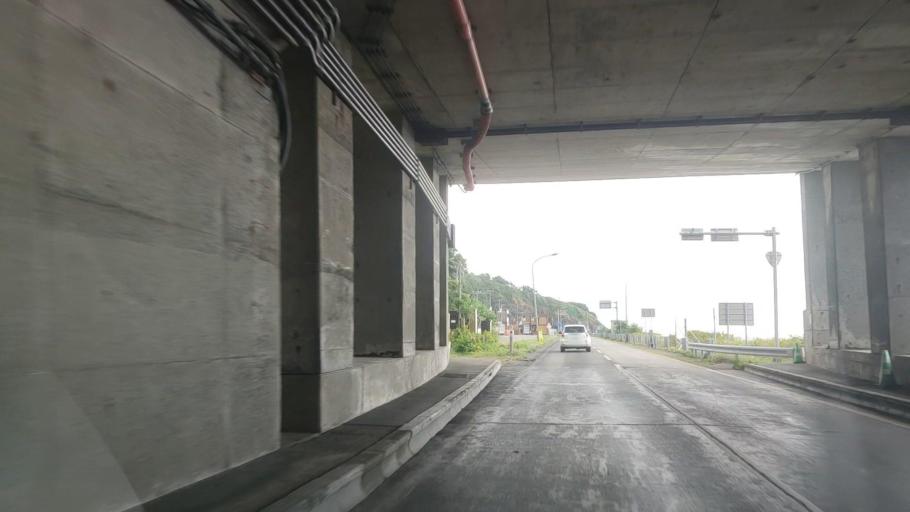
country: JP
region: Hokkaido
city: Rumoi
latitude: 43.7895
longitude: 141.3721
